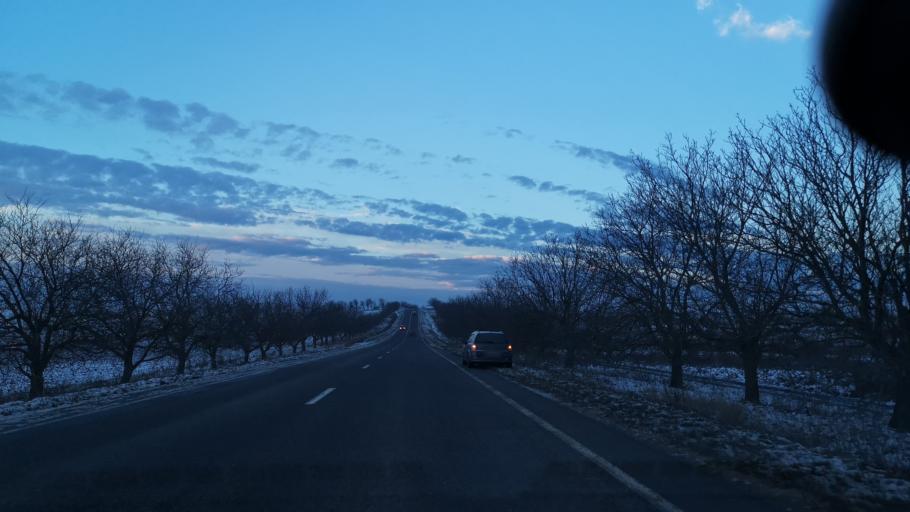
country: MD
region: Rezina
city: Saharna
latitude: 47.6207
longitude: 28.8332
